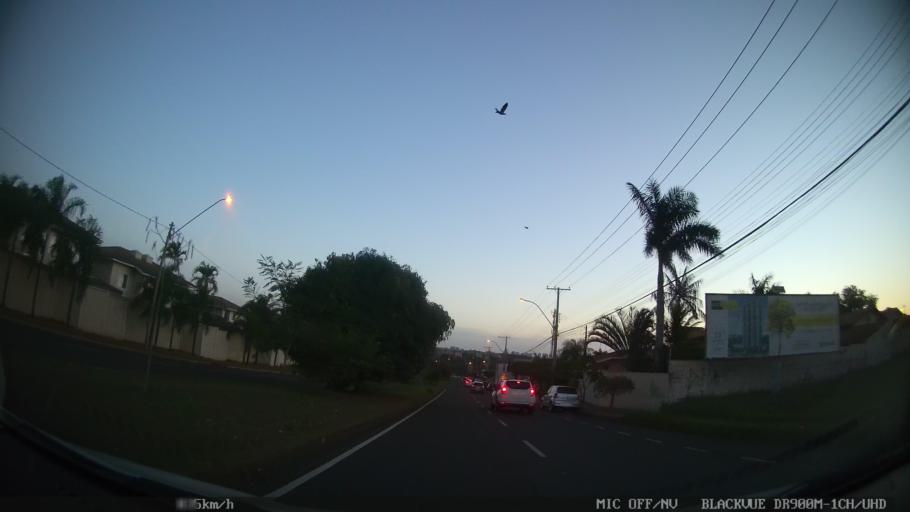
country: BR
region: Sao Paulo
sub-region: Sao Jose Do Rio Preto
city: Sao Jose do Rio Preto
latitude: -20.8086
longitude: -49.3500
